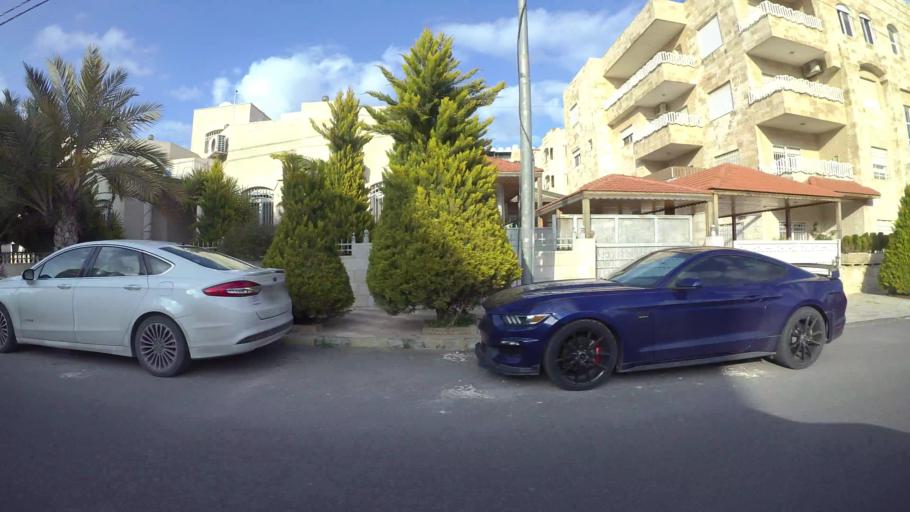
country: JO
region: Amman
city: Al Jubayhah
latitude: 31.9843
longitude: 35.8570
